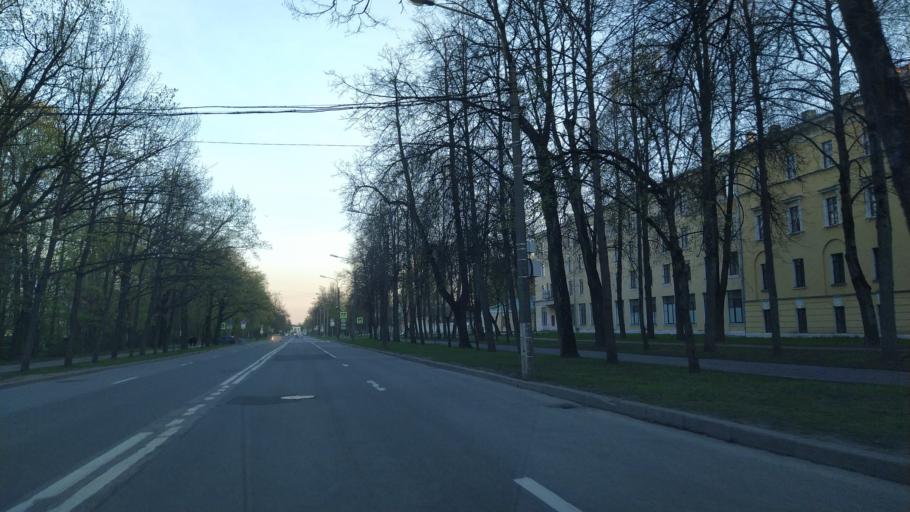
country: RU
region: St.-Petersburg
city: Pushkin
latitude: 59.7091
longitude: 30.4031
